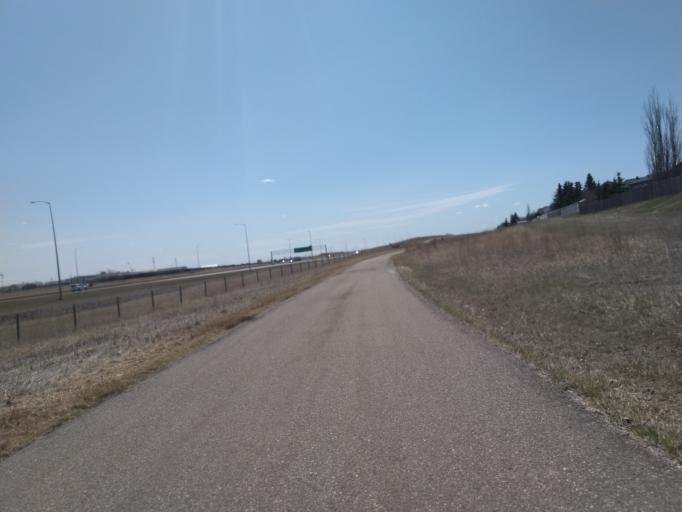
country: CA
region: Alberta
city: Chestermere
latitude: 51.0785
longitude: -113.9228
